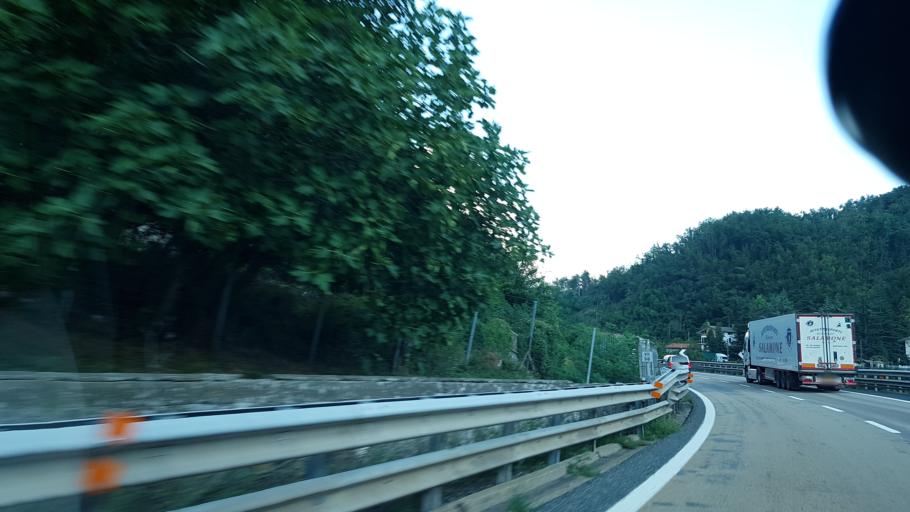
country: IT
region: Liguria
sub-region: Provincia di Genova
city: Isola del Cantone
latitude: 44.6522
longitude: 8.9489
